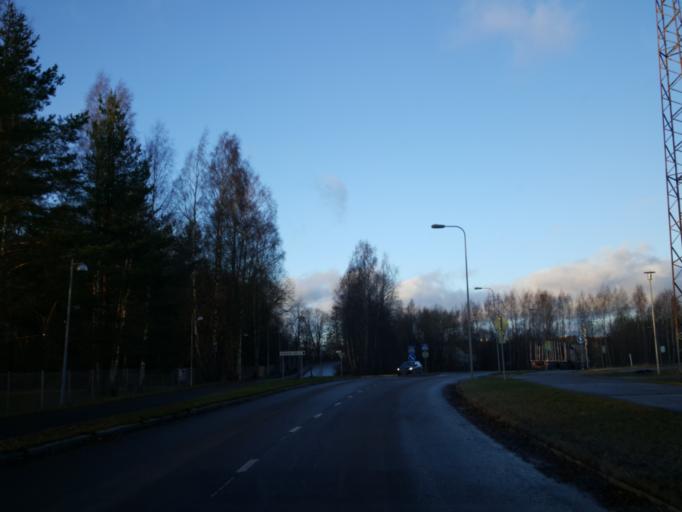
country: FI
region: Uusimaa
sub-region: Helsinki
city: Lohja
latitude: 60.2573
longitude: 24.0601
